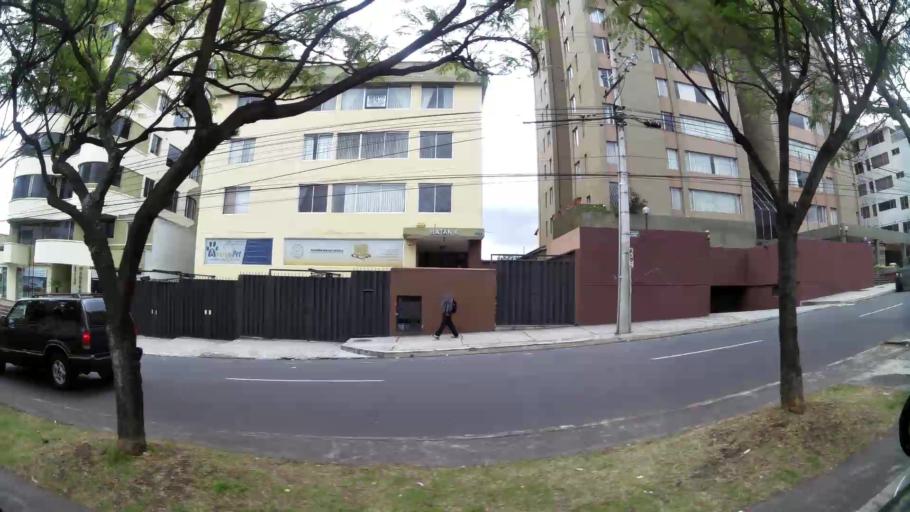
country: EC
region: Pichincha
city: Quito
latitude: -0.1713
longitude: -78.4745
